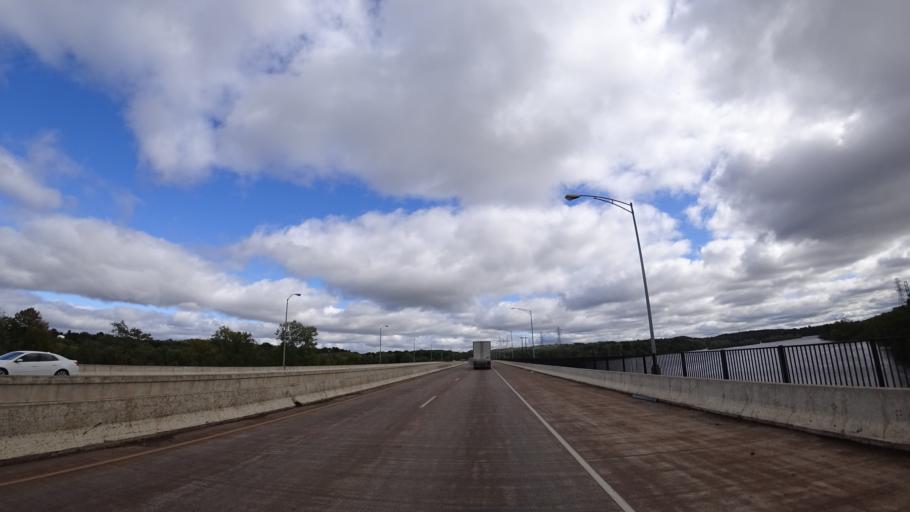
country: US
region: Wisconsin
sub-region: Eau Claire County
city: Eau Claire
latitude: 44.8409
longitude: -91.5018
